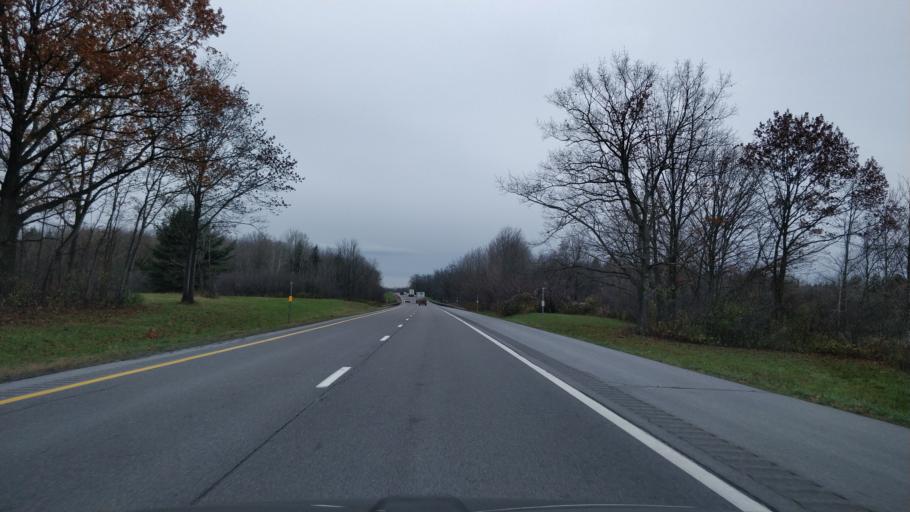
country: US
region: New York
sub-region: Oswego County
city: Pulaski
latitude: 43.6085
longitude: -76.0935
